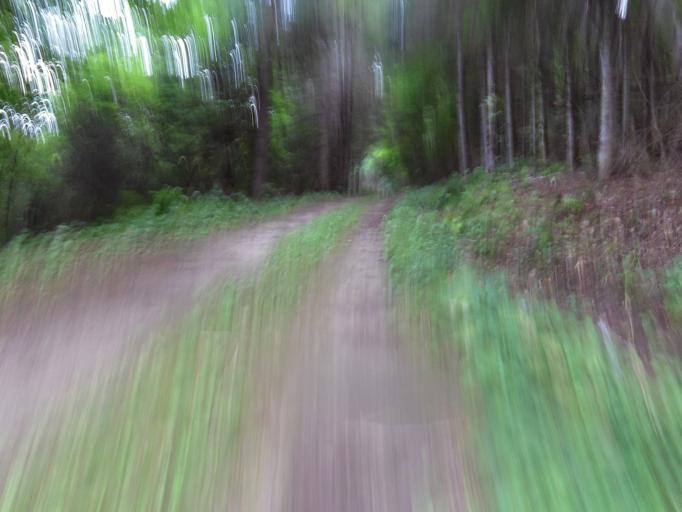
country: CA
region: Quebec
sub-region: Outaouais
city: Wakefield
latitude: 45.6371
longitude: -75.9908
